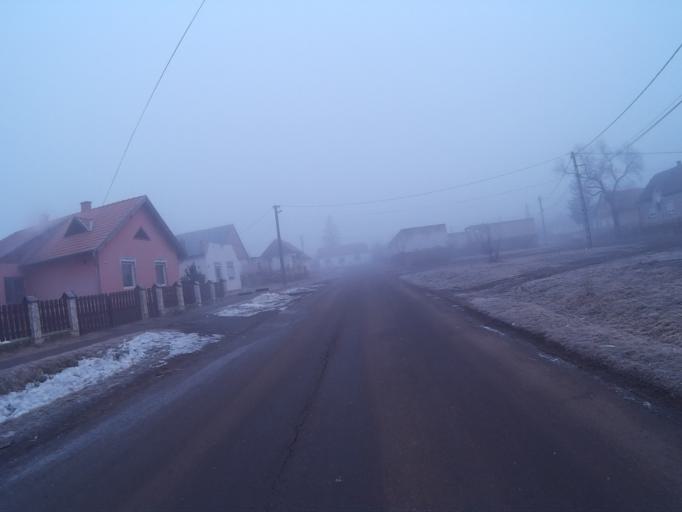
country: HU
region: Nograd
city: Matraverebely
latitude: 47.9764
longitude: 19.7758
